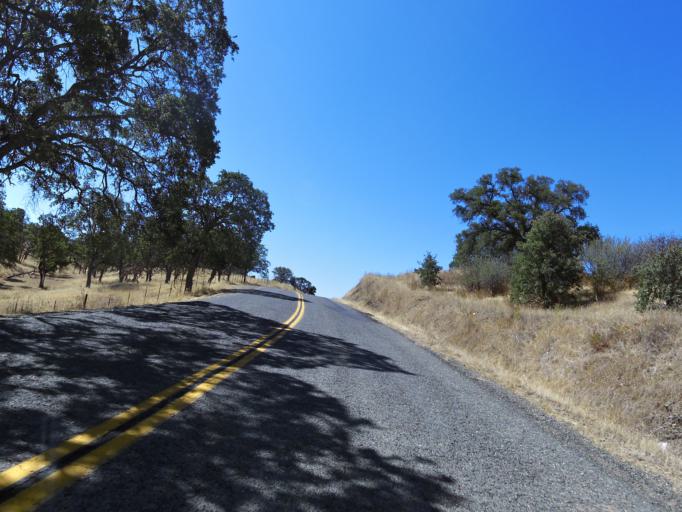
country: US
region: California
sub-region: Tuolumne County
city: Tuolumne City
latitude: 37.6668
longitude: -120.3153
